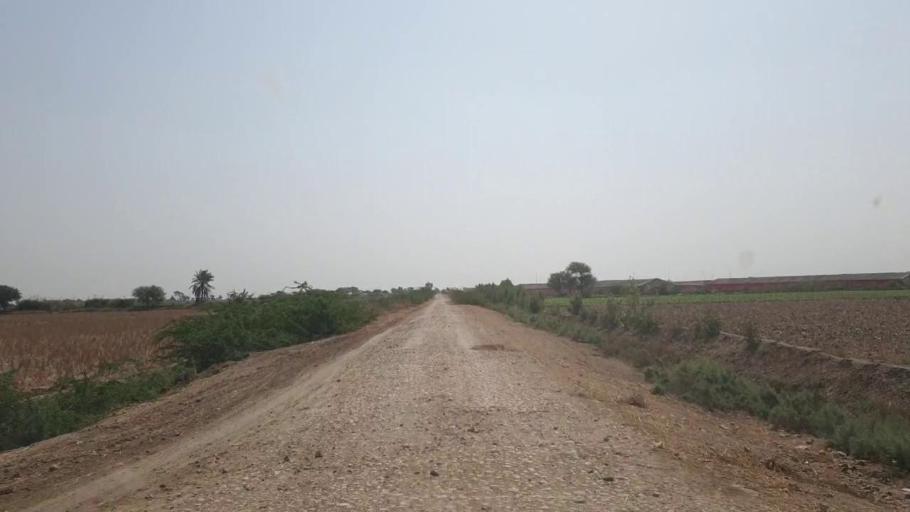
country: PK
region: Sindh
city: Jati
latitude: 24.4267
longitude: 68.5524
